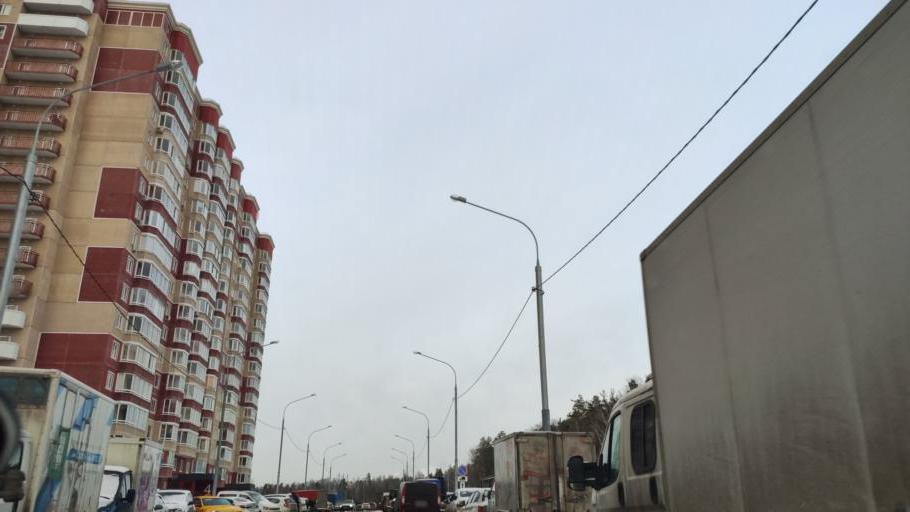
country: RU
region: Moscow
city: Annino
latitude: 55.5333
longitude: 37.6212
